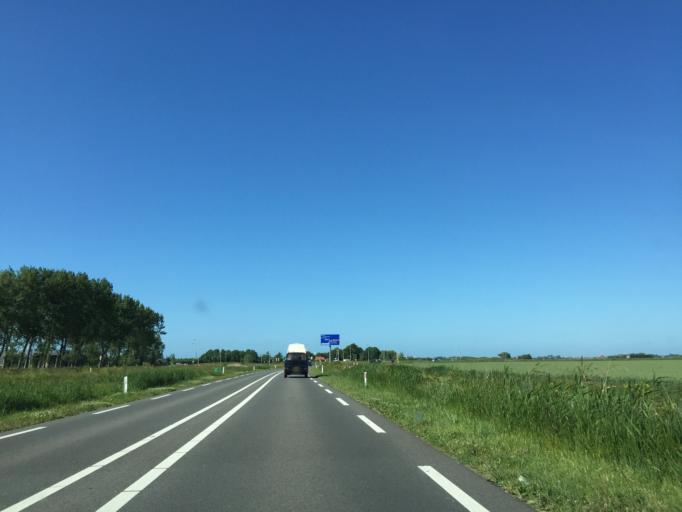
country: NL
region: Zeeland
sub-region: Schouwen-Duiveland
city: Haamstede
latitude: 51.6949
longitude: 3.7511
